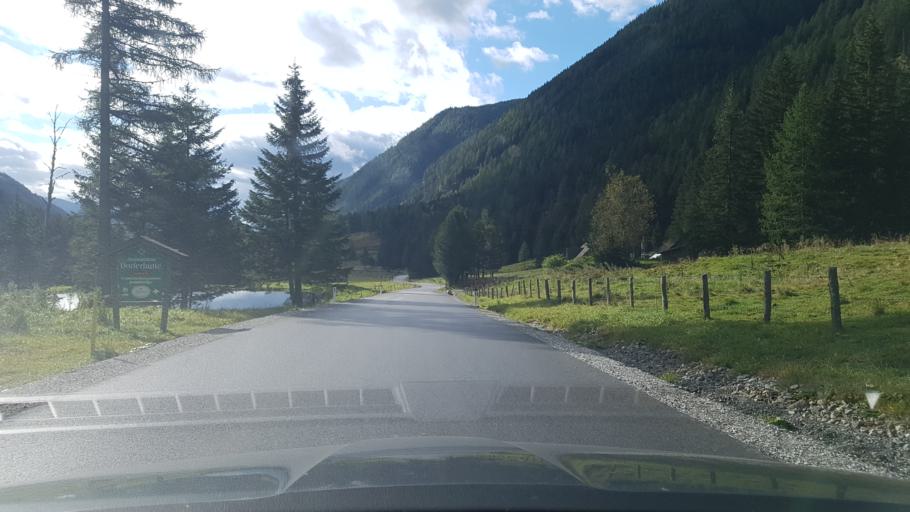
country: AT
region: Styria
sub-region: Politischer Bezirk Murau
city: Schoder
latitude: 47.2431
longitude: 14.0823
